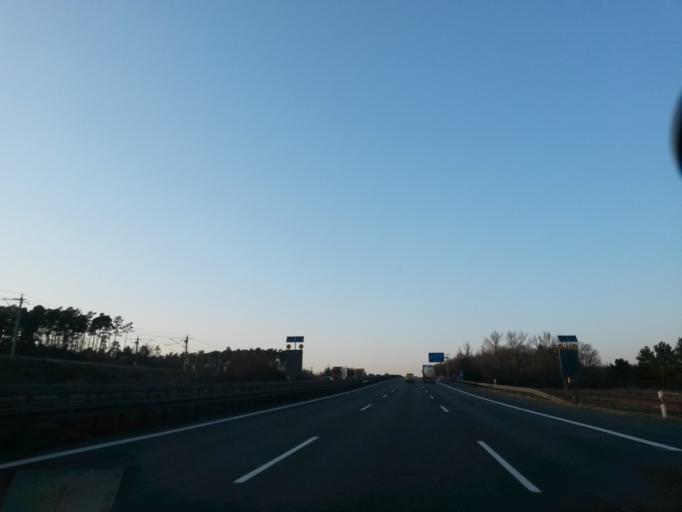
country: DE
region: Bavaria
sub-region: Regierungsbezirk Mittelfranken
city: Allersberg
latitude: 49.2463
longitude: 11.2172
